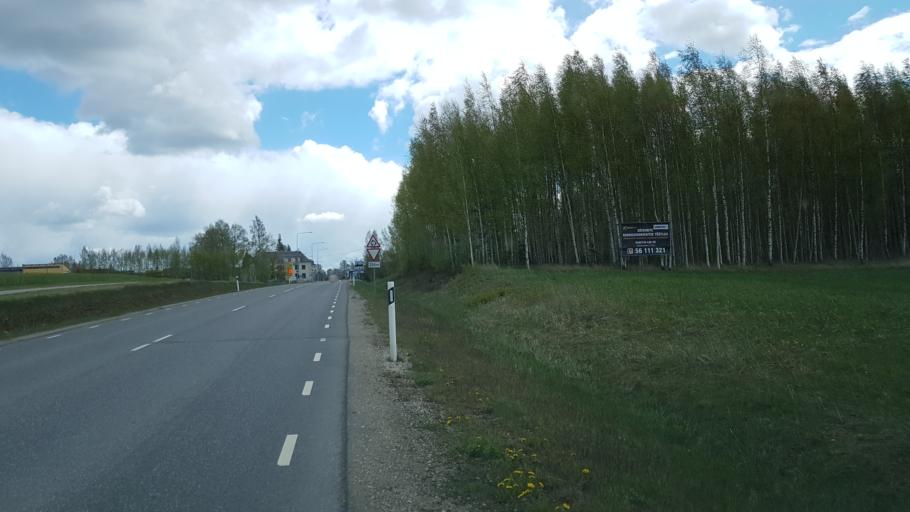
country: EE
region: Jaervamaa
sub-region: Tueri vald
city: Tueri
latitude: 58.8150
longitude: 25.3995
